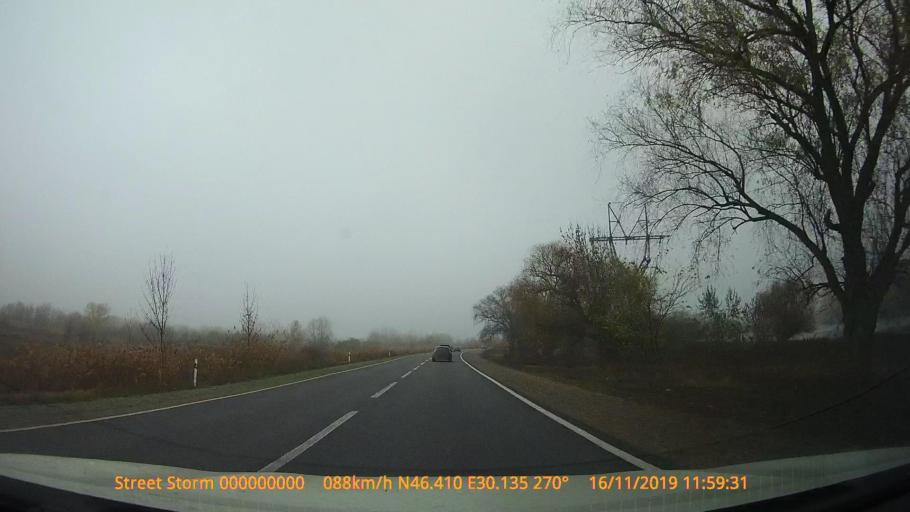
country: UA
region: Odessa
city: Bilyayivka
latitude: 46.4103
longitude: 30.1349
